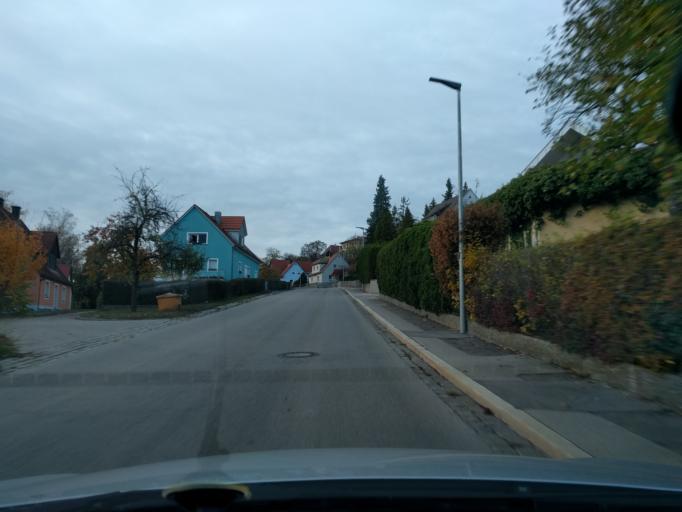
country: DE
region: Bavaria
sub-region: Regierungsbezirk Mittelfranken
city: Herrieden
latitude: 49.2375
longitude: 10.4918
